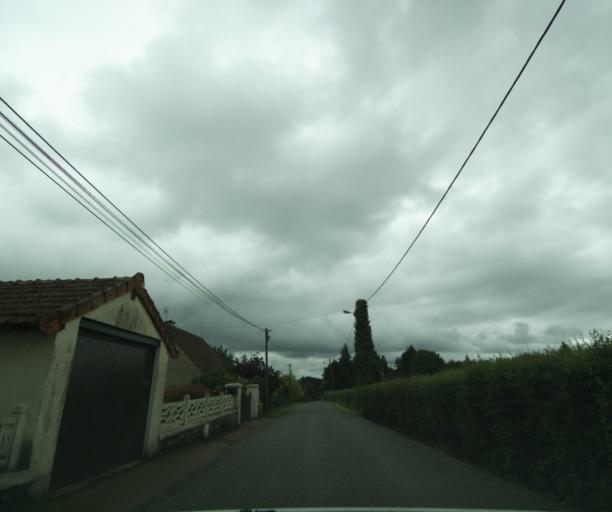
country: FR
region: Bourgogne
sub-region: Departement de Saone-et-Loire
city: Charolles
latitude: 46.4407
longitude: 4.2783
